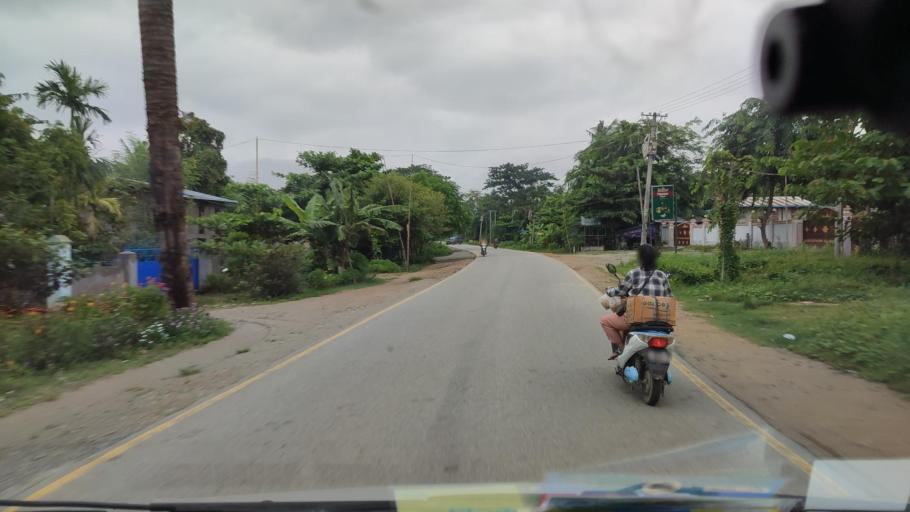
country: MM
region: Bago
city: Taungoo
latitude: 18.9495
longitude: 96.4725
